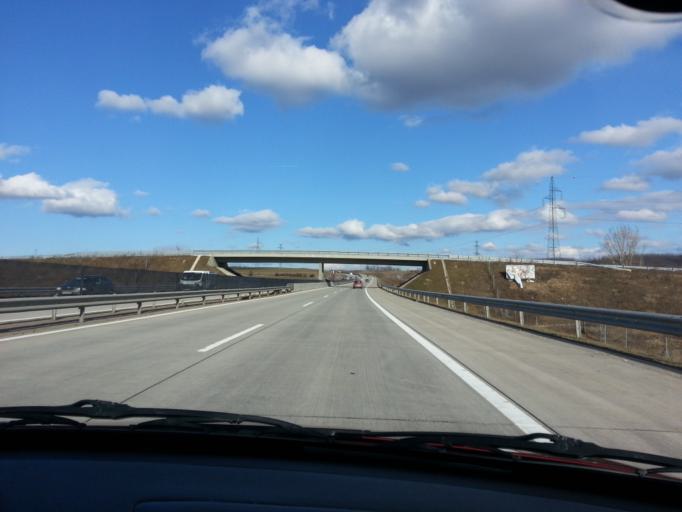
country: HU
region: Pest
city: Nagytarcsa
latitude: 47.5408
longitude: 19.3083
